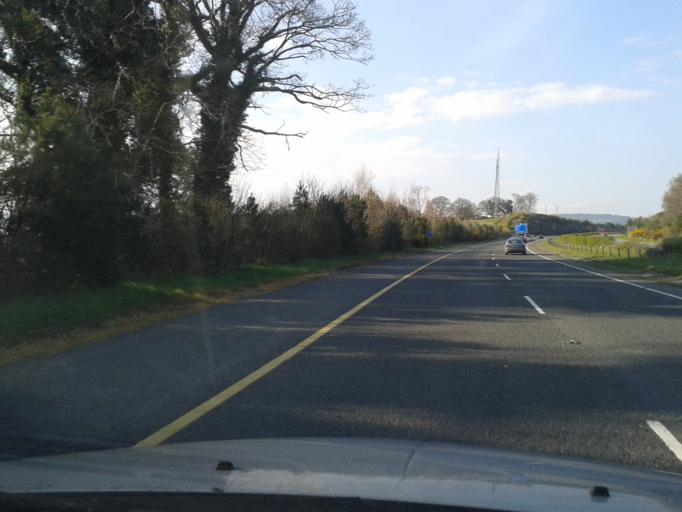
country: IE
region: Leinster
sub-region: Wicklow
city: Ashford
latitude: 53.0117
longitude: -6.0988
